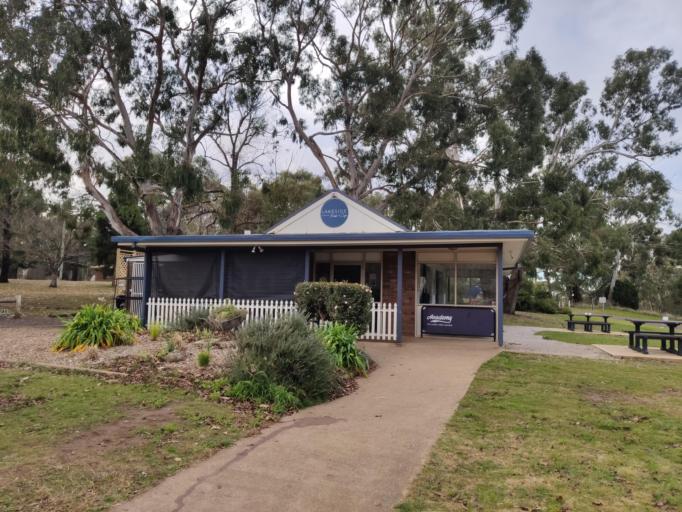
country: AU
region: New South Wales
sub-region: Orange Municipality
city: Orange
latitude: -33.3014
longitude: 149.0274
